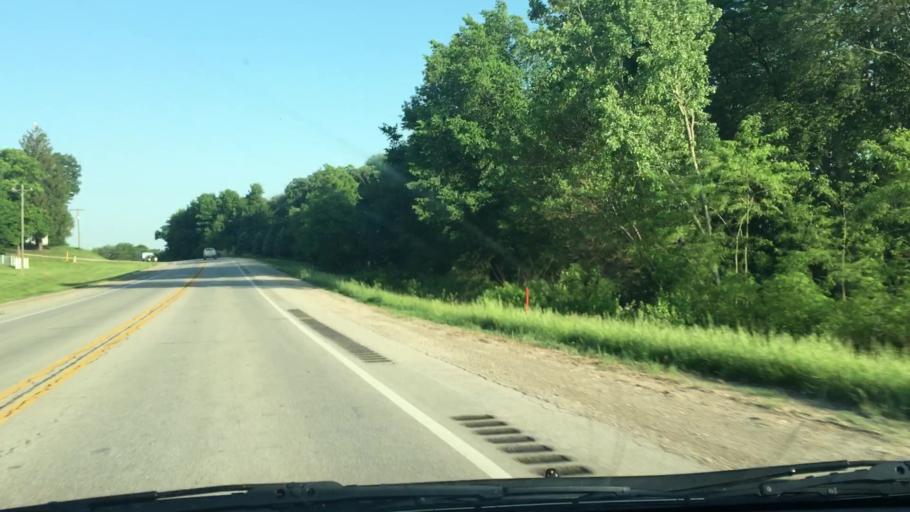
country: US
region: Iowa
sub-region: Johnson County
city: Tiffin
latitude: 41.7105
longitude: -91.6909
